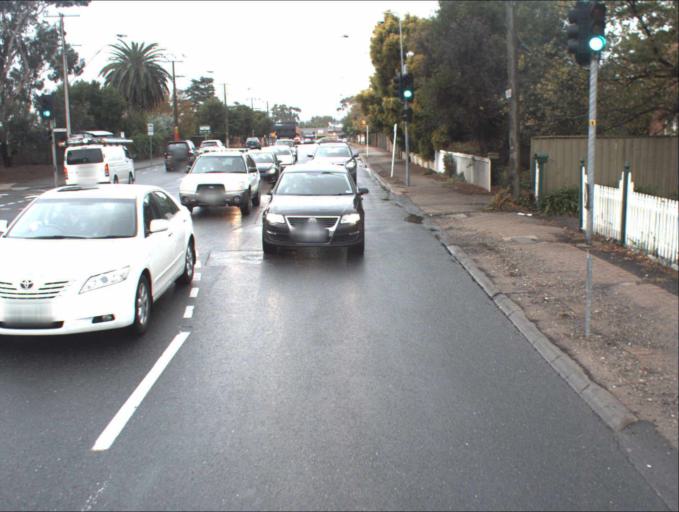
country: AU
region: South Australia
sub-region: Port Adelaide Enfield
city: Klemzig
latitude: -34.8818
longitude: 138.6198
